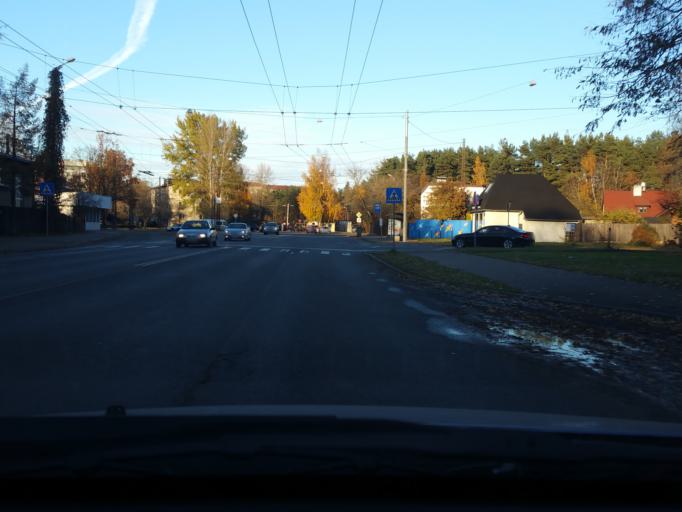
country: LV
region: Riga
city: Jaunciems
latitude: 56.9645
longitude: 24.1949
